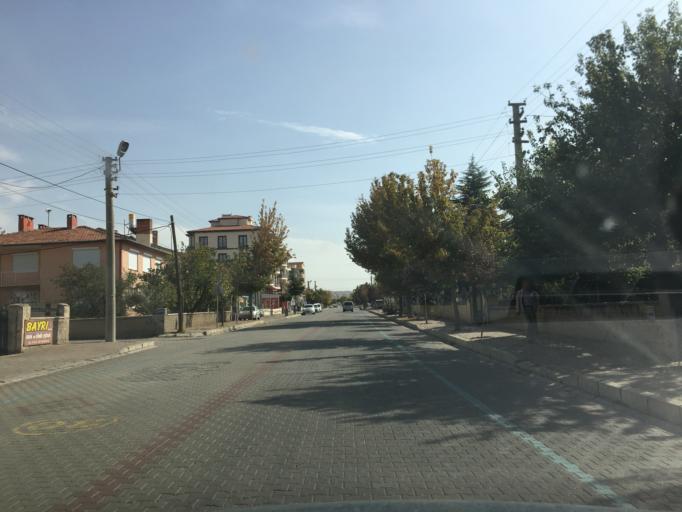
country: TR
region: Nevsehir
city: Avanos
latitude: 38.7084
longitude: 34.8509
